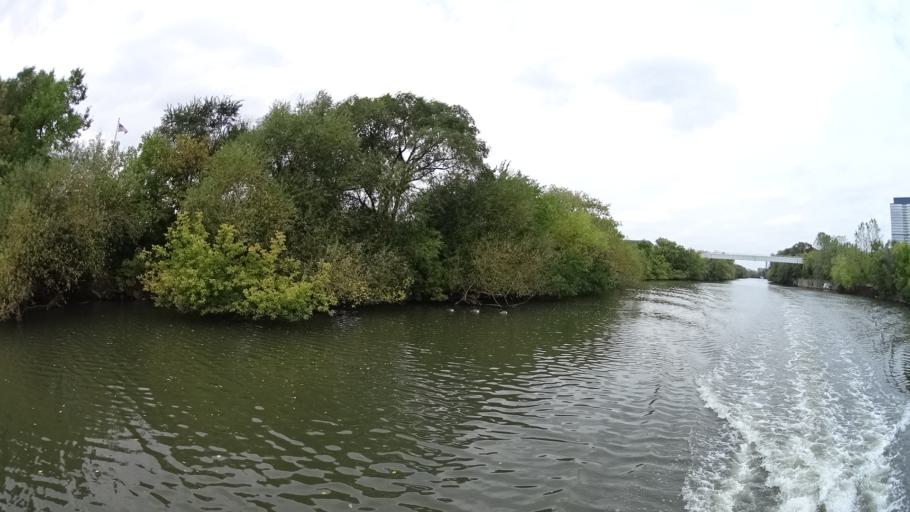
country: US
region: Illinois
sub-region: Cook County
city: Chicago
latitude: 41.9041
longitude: -87.6499
